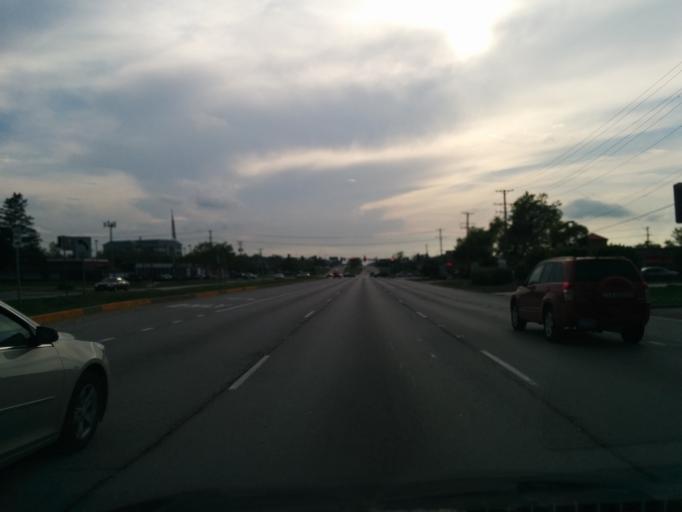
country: US
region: Illinois
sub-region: DuPage County
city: Lombard
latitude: 41.9045
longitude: -88.0302
